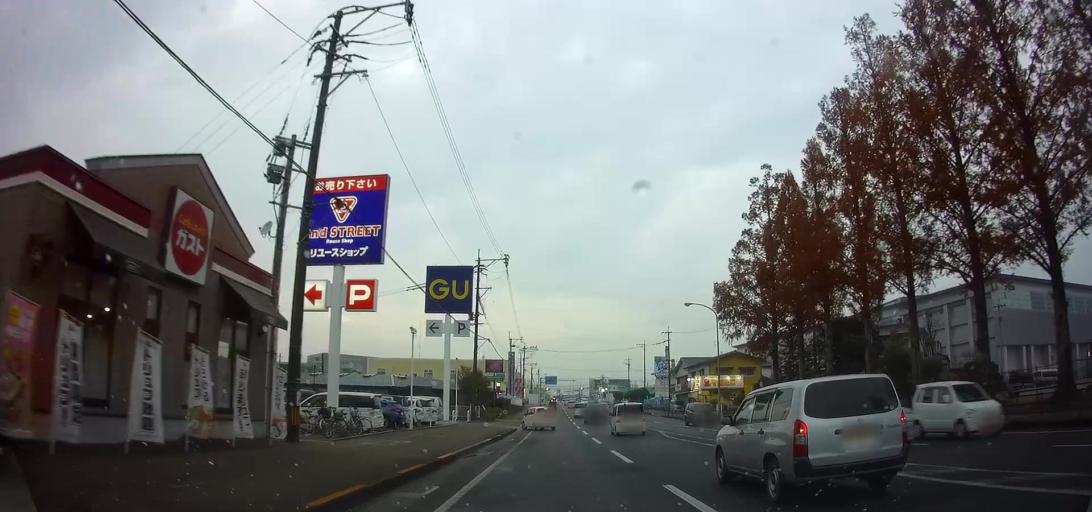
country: JP
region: Nagasaki
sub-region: Isahaya-shi
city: Isahaya
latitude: 32.8384
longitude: 130.0364
